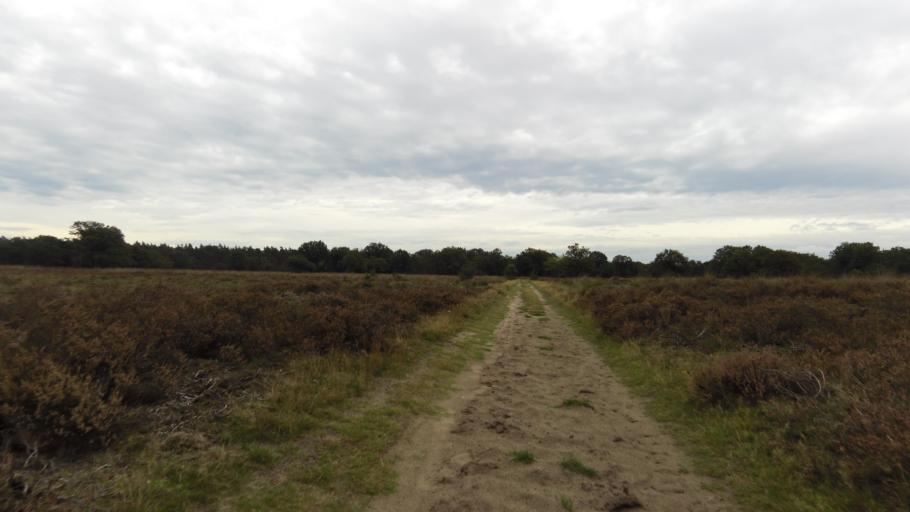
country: NL
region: Gelderland
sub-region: Gemeente Barneveld
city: Garderen
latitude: 52.1905
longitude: 5.7407
